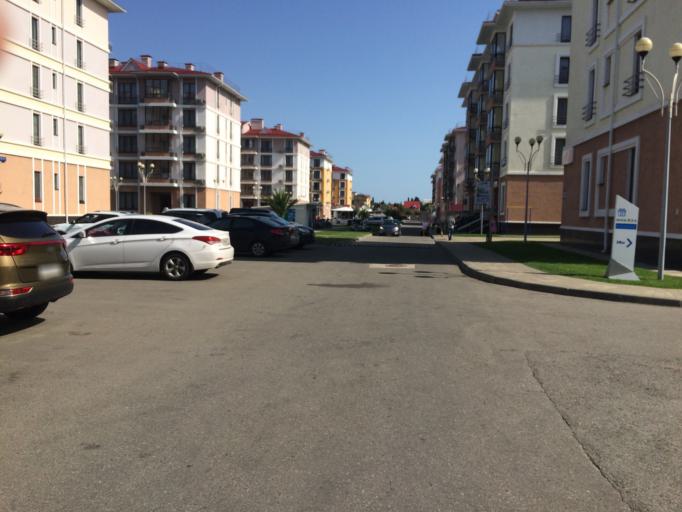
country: RU
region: Krasnodarskiy
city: Adler
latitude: 43.3970
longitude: 39.9761
